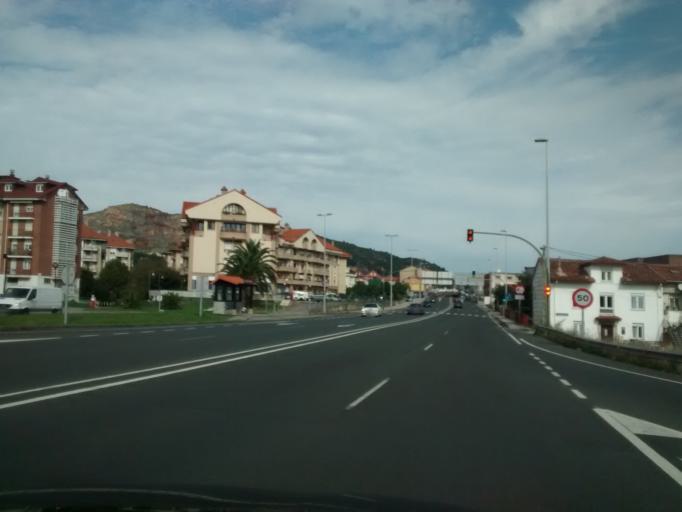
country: ES
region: Cantabria
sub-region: Provincia de Cantabria
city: Camargo
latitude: 43.4403
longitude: -3.8600
